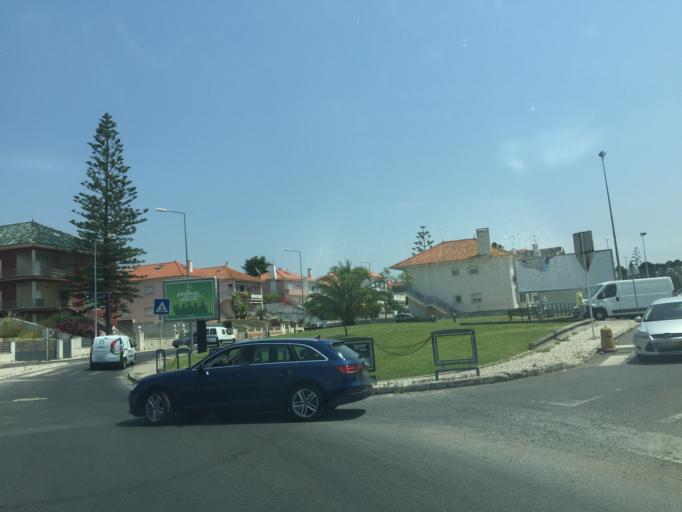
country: PT
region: Lisbon
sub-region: Loures
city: Loures
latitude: 38.8368
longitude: -9.1689
